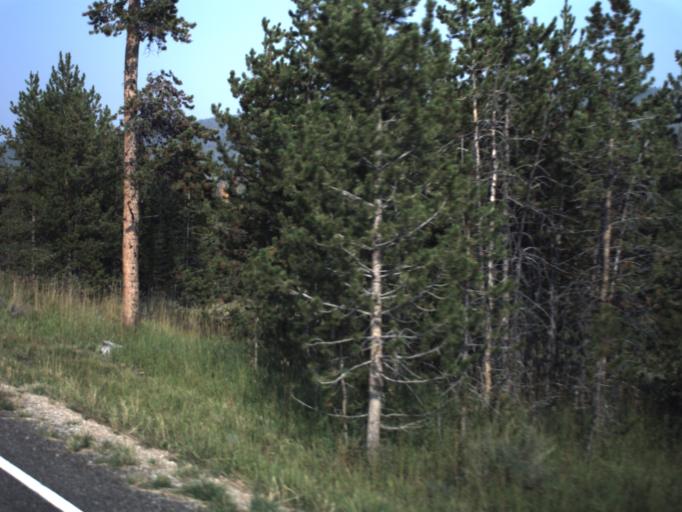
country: US
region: Wyoming
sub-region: Uinta County
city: Evanston
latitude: 40.8591
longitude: -110.8423
